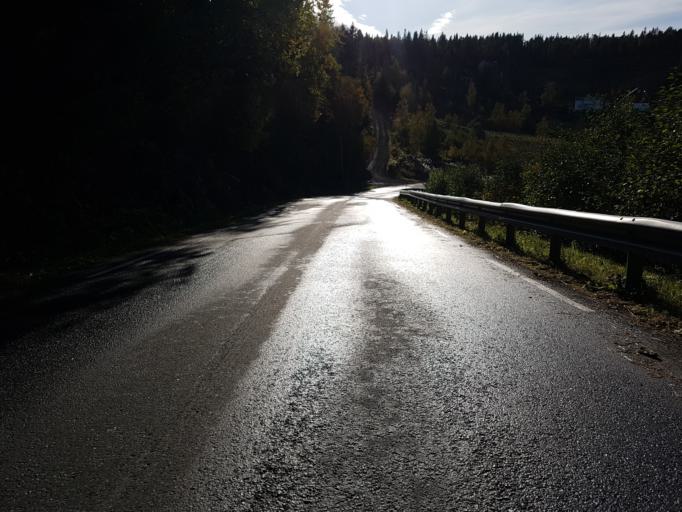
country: NO
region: Sor-Trondelag
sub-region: Klaebu
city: Klaebu
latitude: 63.3402
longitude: 10.5655
